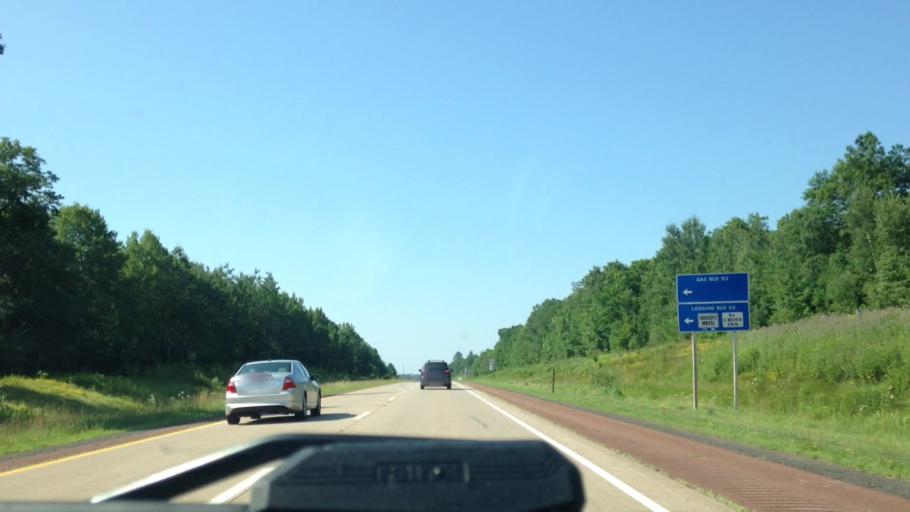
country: US
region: Wisconsin
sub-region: Douglas County
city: Lake Nebagamon
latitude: 46.3868
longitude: -91.8205
